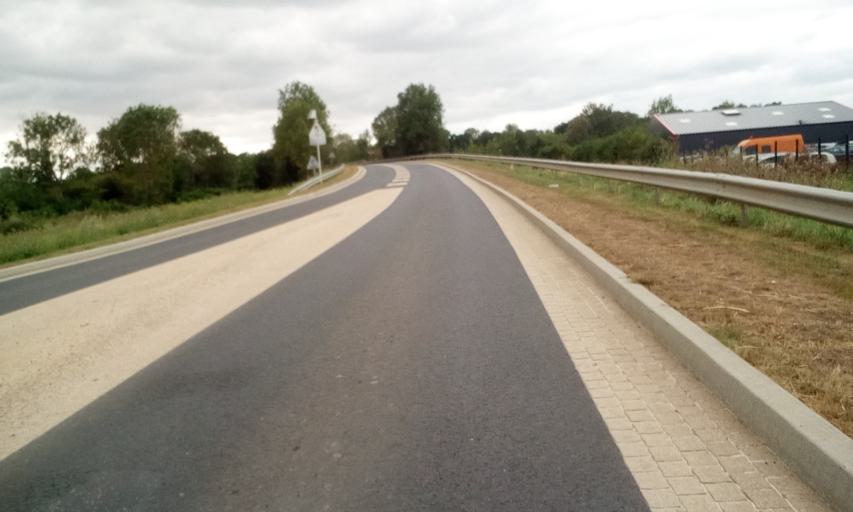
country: FR
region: Lower Normandy
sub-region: Departement du Calvados
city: Troarn
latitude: 49.1875
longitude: -0.1899
